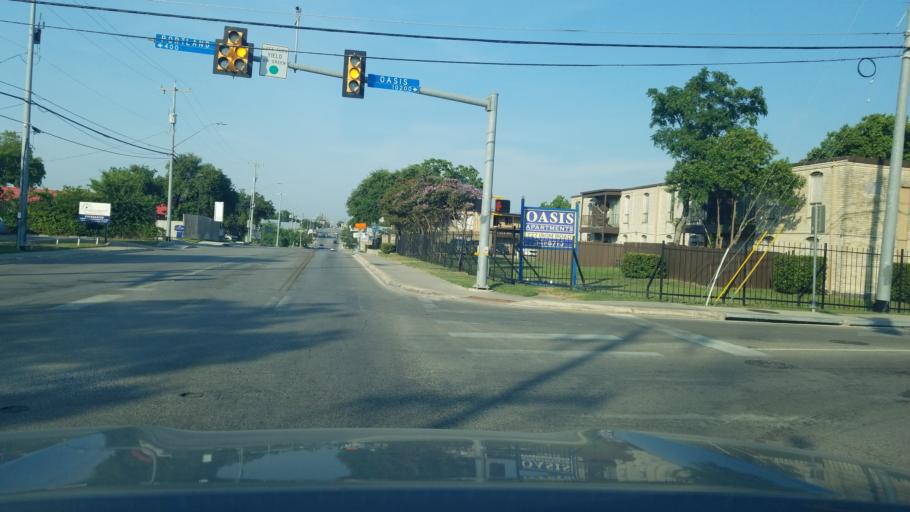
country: US
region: Texas
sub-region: Bexar County
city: Castle Hills
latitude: 29.5323
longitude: -98.4889
